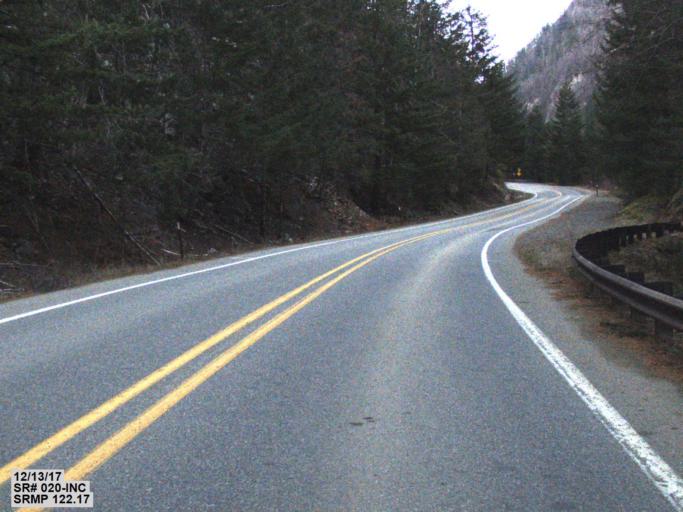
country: US
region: Washington
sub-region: Snohomish County
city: Darrington
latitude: 48.6894
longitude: -121.2305
